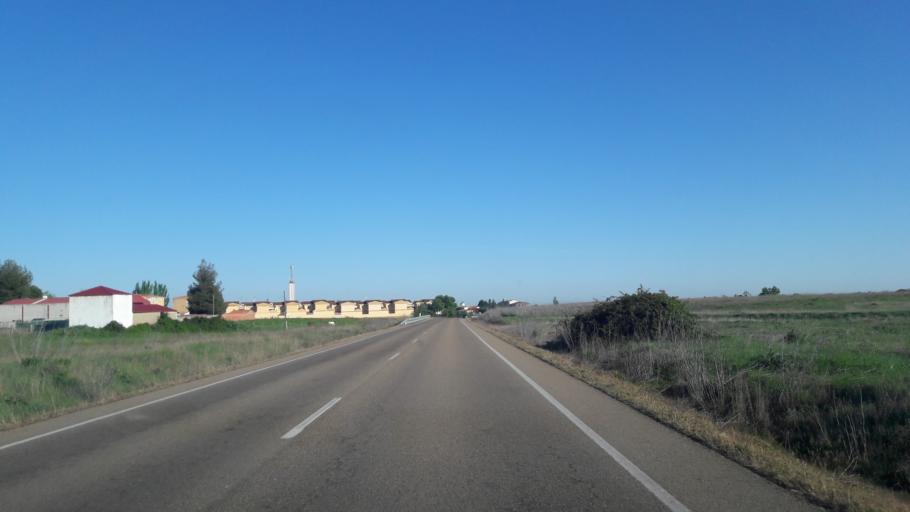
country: ES
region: Castille and Leon
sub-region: Provincia de Salamanca
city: La Fuente de San Esteban
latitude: 40.7975
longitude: -6.2504
